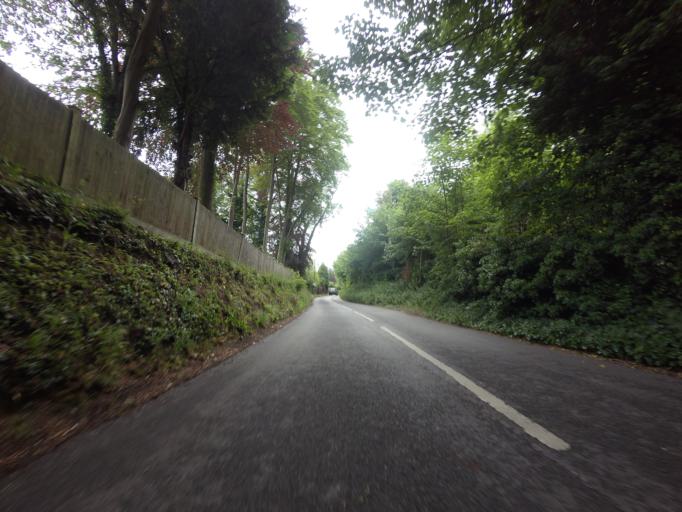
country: GB
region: England
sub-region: Kent
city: Shoreham
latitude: 51.3403
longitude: 0.1771
